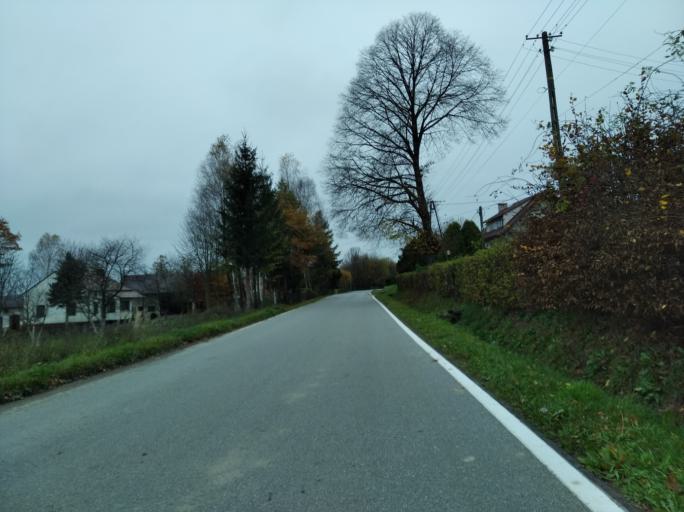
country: PL
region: Subcarpathian Voivodeship
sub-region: Powiat krosnienski
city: Leki
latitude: 49.8175
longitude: 21.6505
